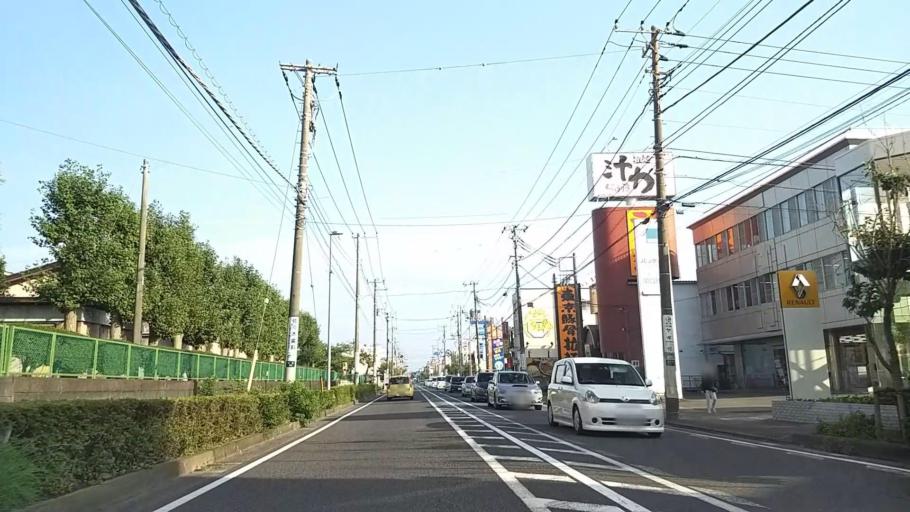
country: JP
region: Kanagawa
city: Hiratsuka
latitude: 35.3313
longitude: 139.3270
